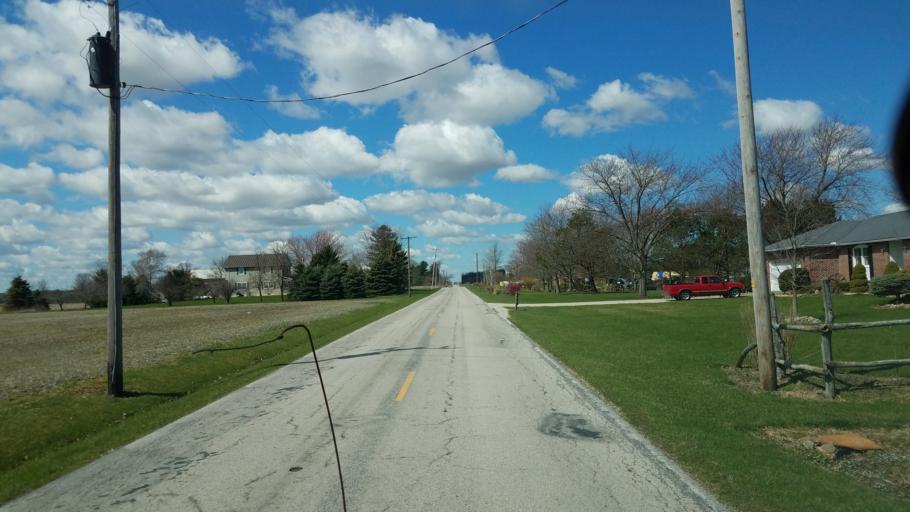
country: US
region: Ohio
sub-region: Sandusky County
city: Mount Carmel
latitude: 41.2416
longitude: -82.9648
